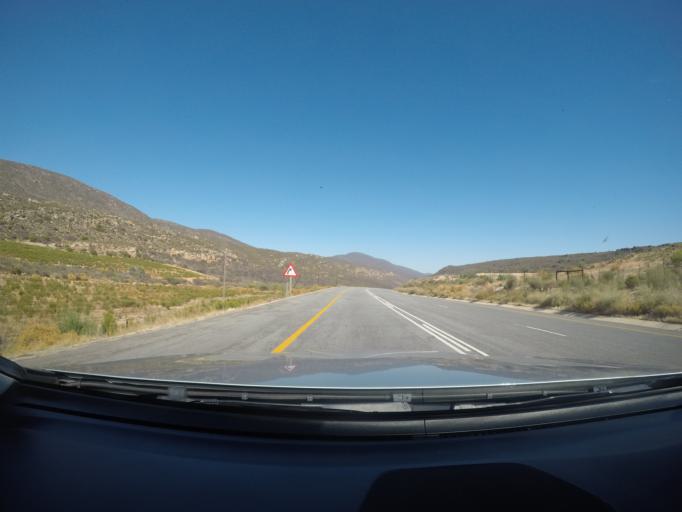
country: ZA
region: Western Cape
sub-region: West Coast District Municipality
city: Clanwilliam
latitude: -32.2657
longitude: 18.8728
